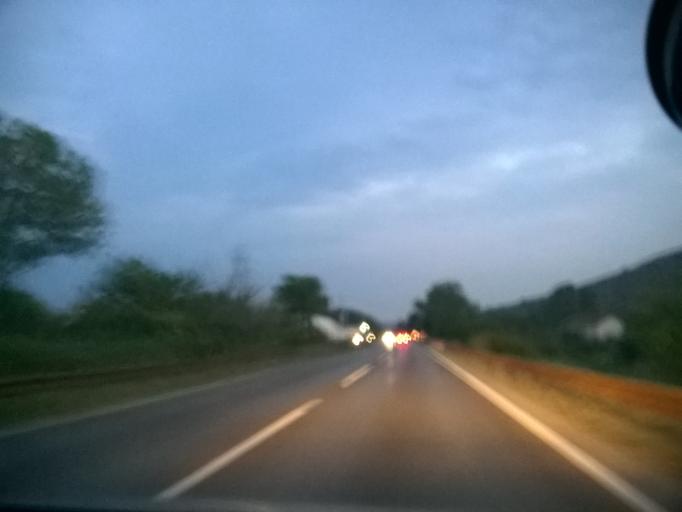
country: ME
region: Danilovgrad
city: Danilovgrad
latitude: 42.5091
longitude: 19.1326
